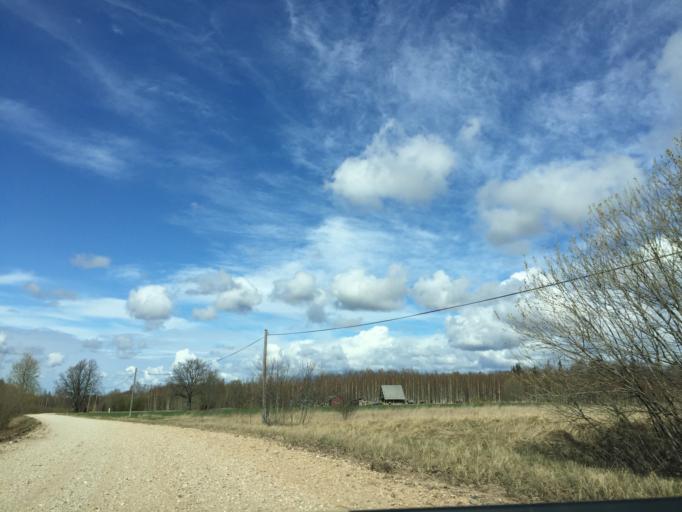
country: LV
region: Limbazu Rajons
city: Limbazi
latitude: 57.5741
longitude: 24.5949
